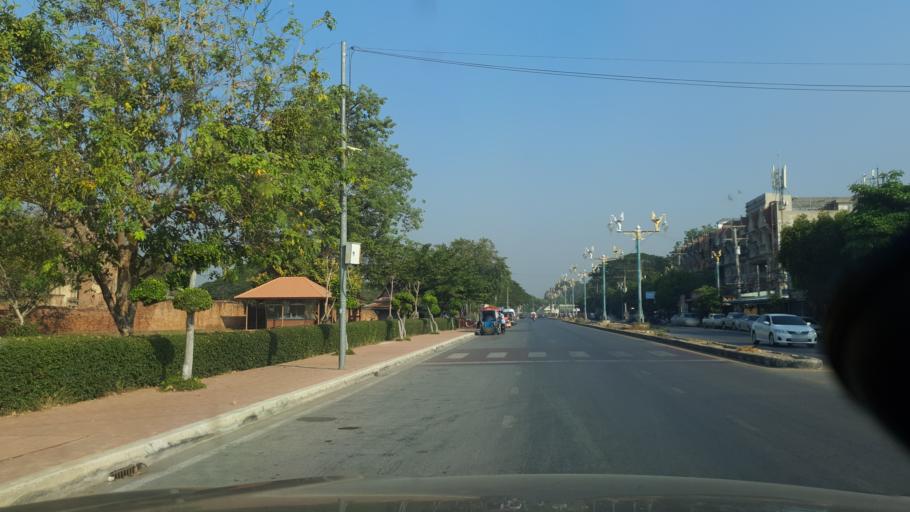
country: TH
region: Phra Nakhon Si Ayutthaya
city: Phra Nakhon Si Ayutthaya
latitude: 14.3582
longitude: 100.5686
